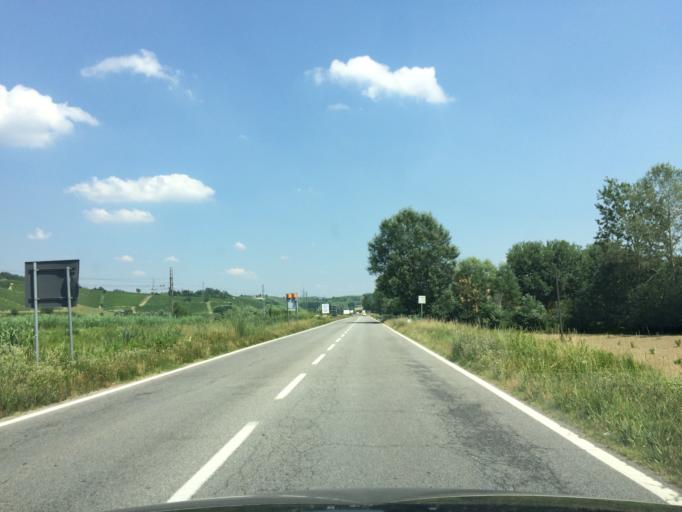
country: IT
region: Piedmont
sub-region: Provincia di Asti
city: Castelnuovo Calcea
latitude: 44.7768
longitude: 8.2818
